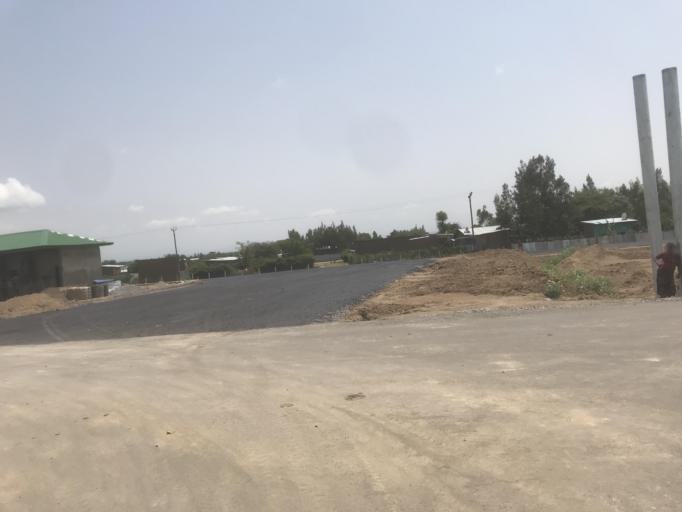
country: ET
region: Oromiya
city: Mojo
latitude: 8.3007
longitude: 38.9403
